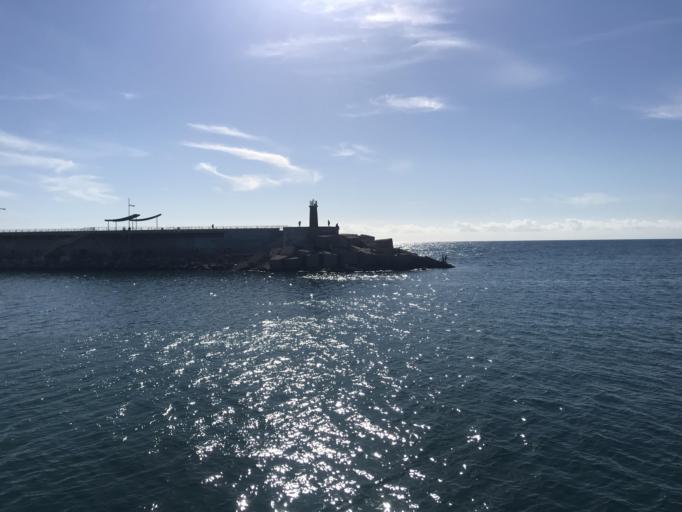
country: ES
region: Valencia
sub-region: Provincia de Alicante
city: Torrevieja
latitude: 37.9653
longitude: -0.6884
